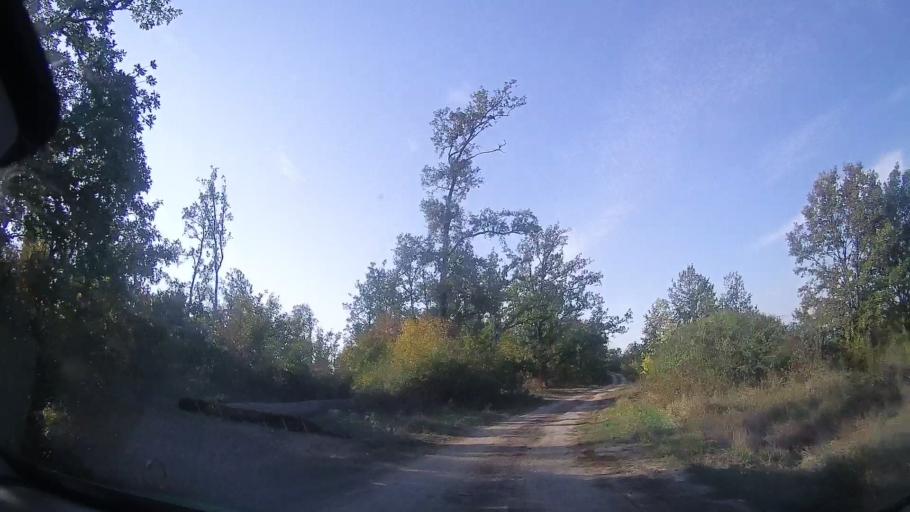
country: RO
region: Timis
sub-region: Comuna Bogda
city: Bogda
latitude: 45.9220
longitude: 21.6134
